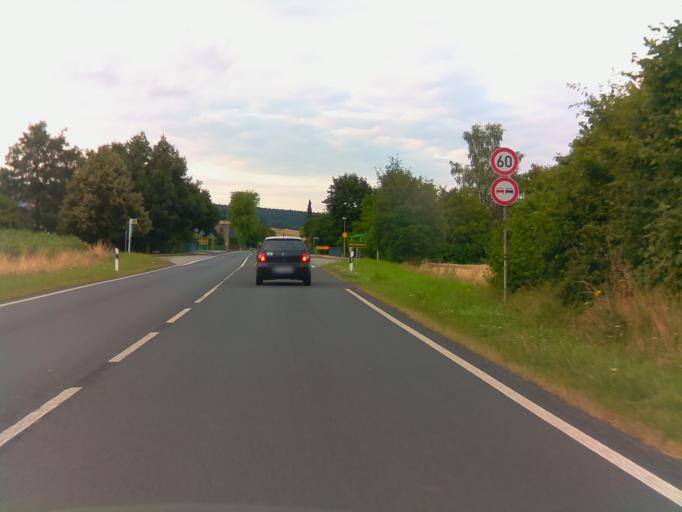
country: DE
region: Hesse
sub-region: Regierungsbezirk Kassel
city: Niederaula
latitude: 50.8229
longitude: 9.6495
